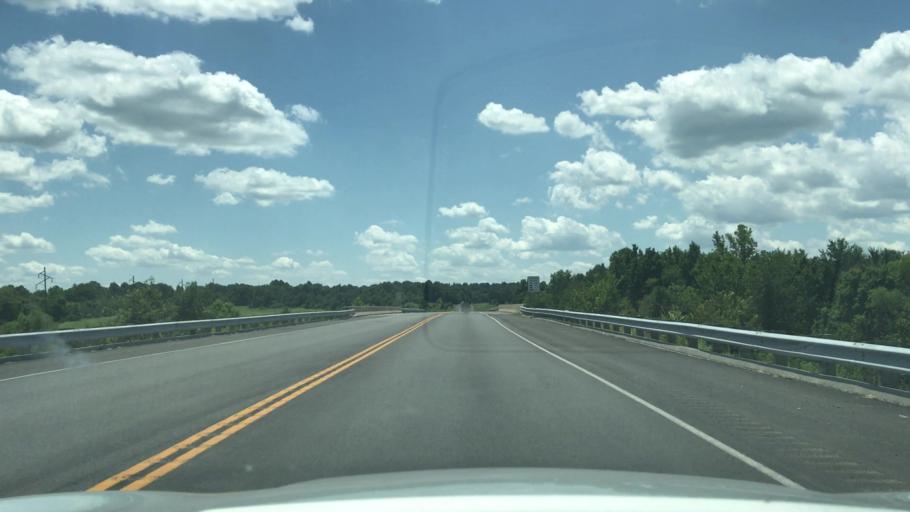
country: US
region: Kentucky
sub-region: Muhlenberg County
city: Greenville
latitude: 37.2139
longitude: -87.1909
